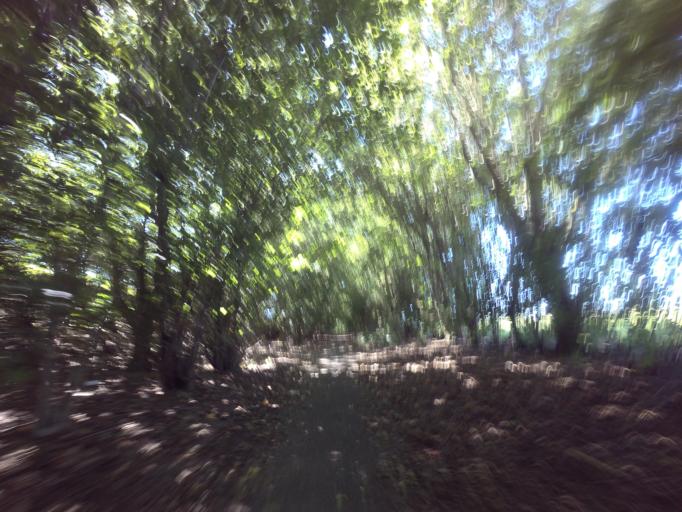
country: GB
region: England
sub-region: Kent
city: Eastry
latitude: 51.2319
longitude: 1.3055
